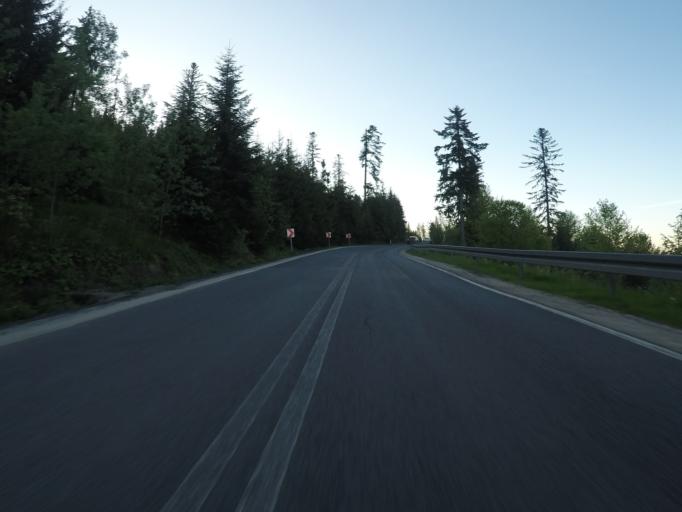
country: PL
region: Lesser Poland Voivodeship
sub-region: Powiat tatrzanski
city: Bukowina Tatrzanska
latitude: 49.2822
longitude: 20.1140
